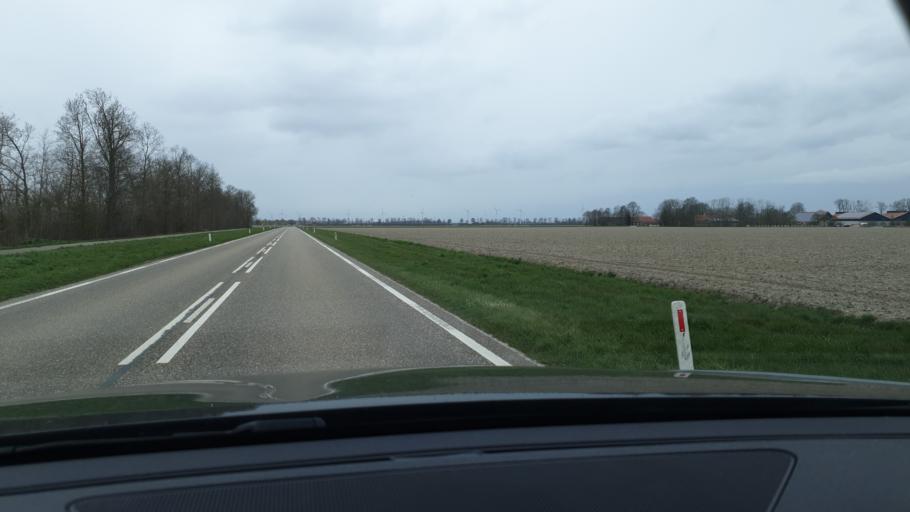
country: NL
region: Flevoland
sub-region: Gemeente Urk
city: Urk
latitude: 52.5669
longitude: 5.6092
